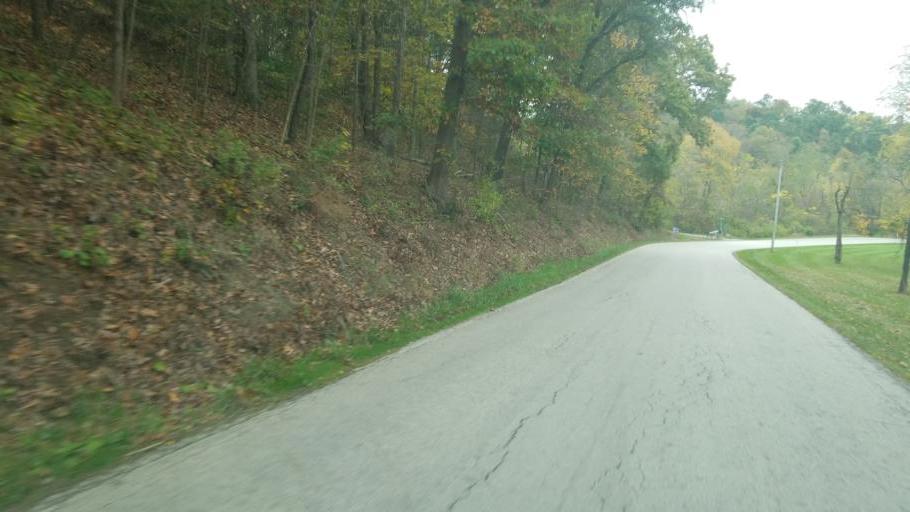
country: US
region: Ohio
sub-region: Ashland County
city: Loudonville
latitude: 40.5595
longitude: -82.1083
